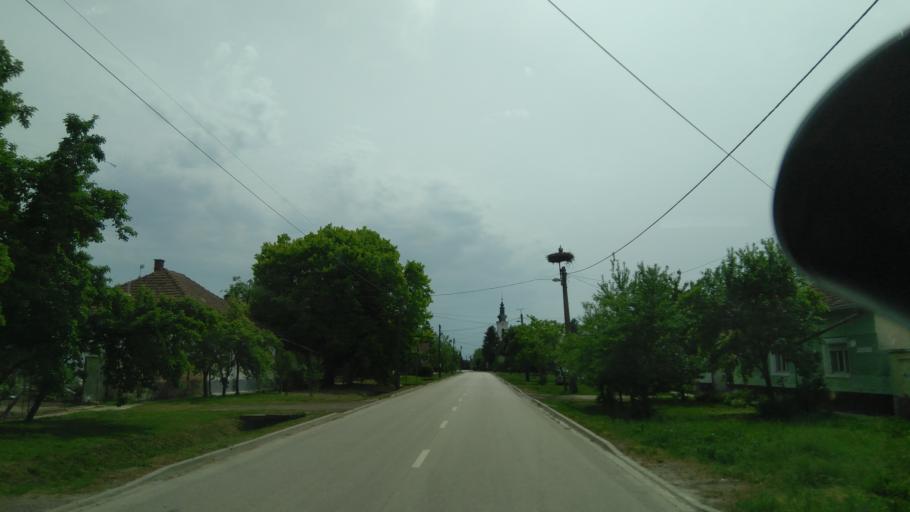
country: HU
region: Bekes
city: Mehkerek
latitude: 46.8714
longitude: 21.5251
